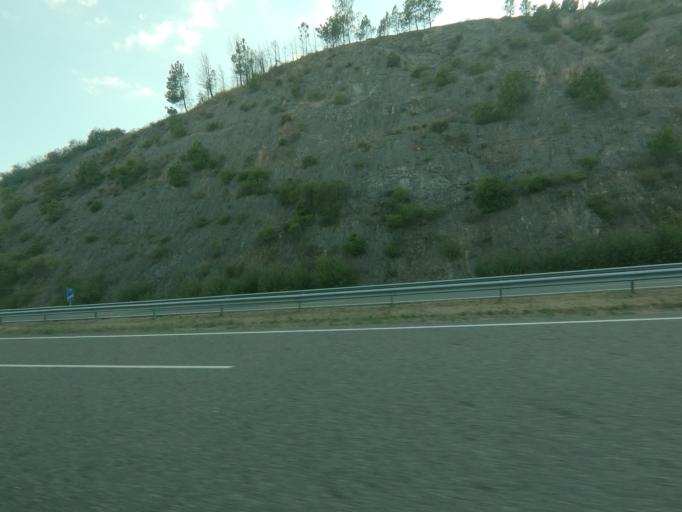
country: ES
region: Galicia
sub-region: Provincia de Ourense
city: Oimbra
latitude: 41.9360
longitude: -7.4989
